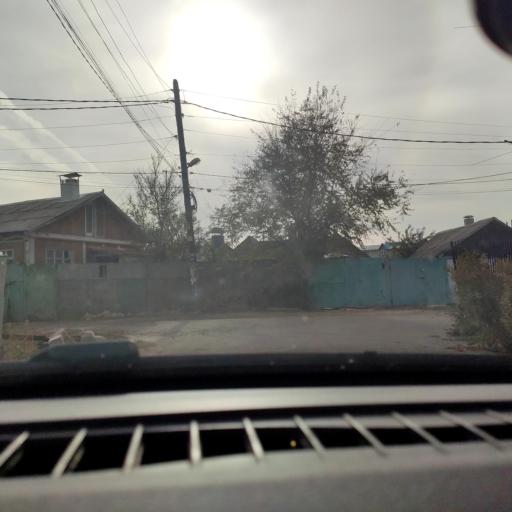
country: RU
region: Voronezj
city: Voronezh
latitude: 51.6486
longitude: 39.1804
